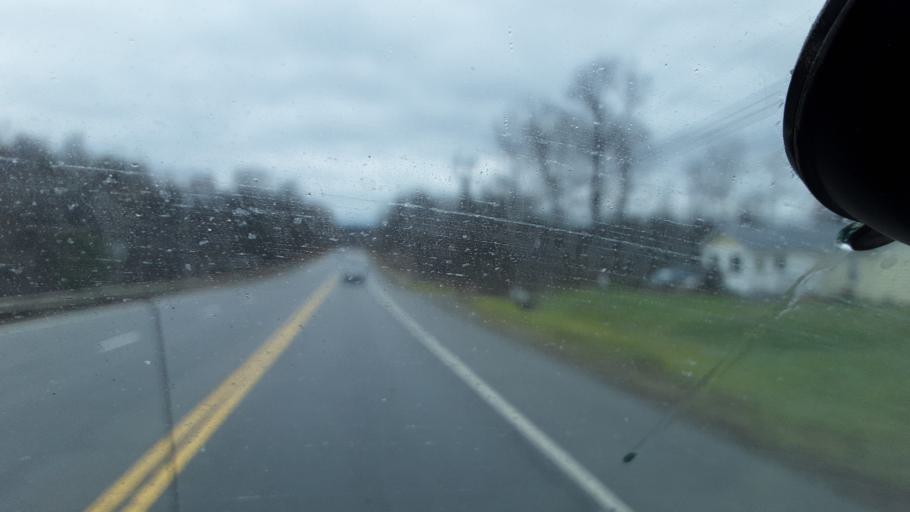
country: US
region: New York
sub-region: Erie County
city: Holland
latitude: 42.5951
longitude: -78.4957
